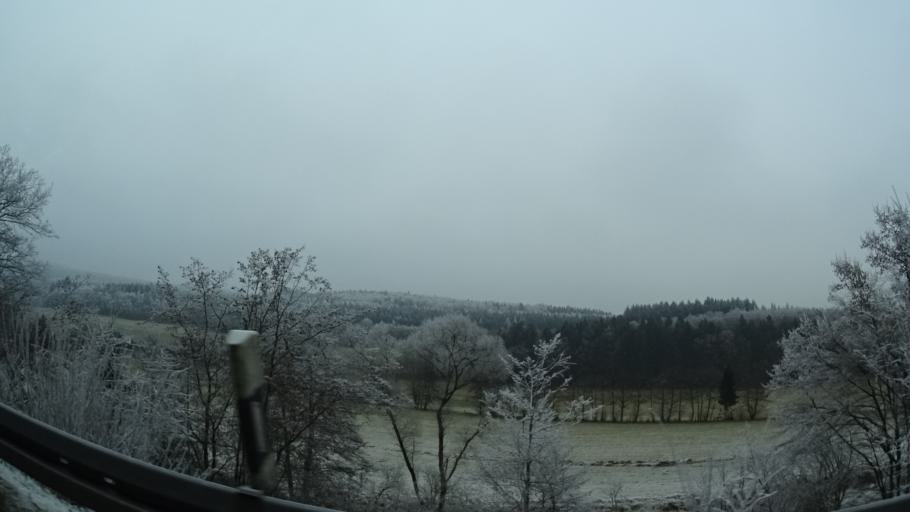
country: DE
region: Bavaria
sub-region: Regierungsbezirk Unterfranken
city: Obersinn
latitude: 50.2586
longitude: 9.5539
